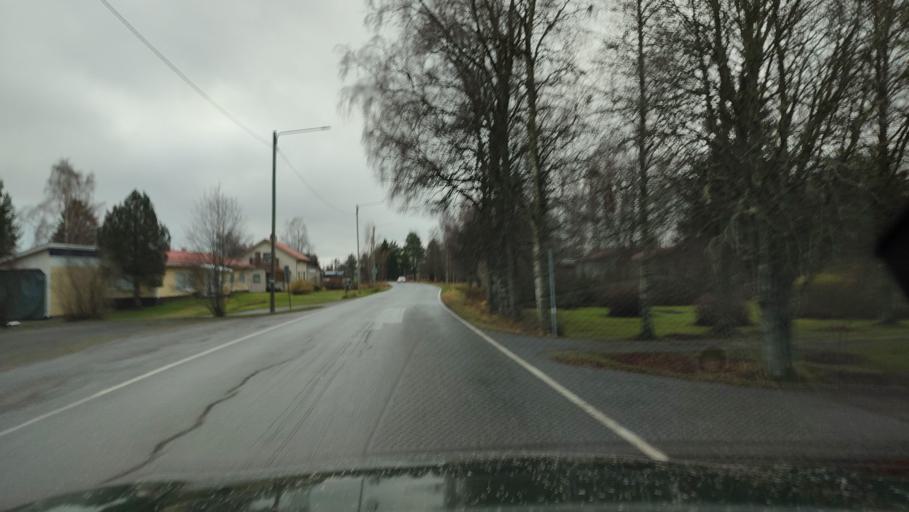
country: FI
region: Southern Ostrobothnia
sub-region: Suupohja
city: Teuva
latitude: 62.4547
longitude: 21.6044
